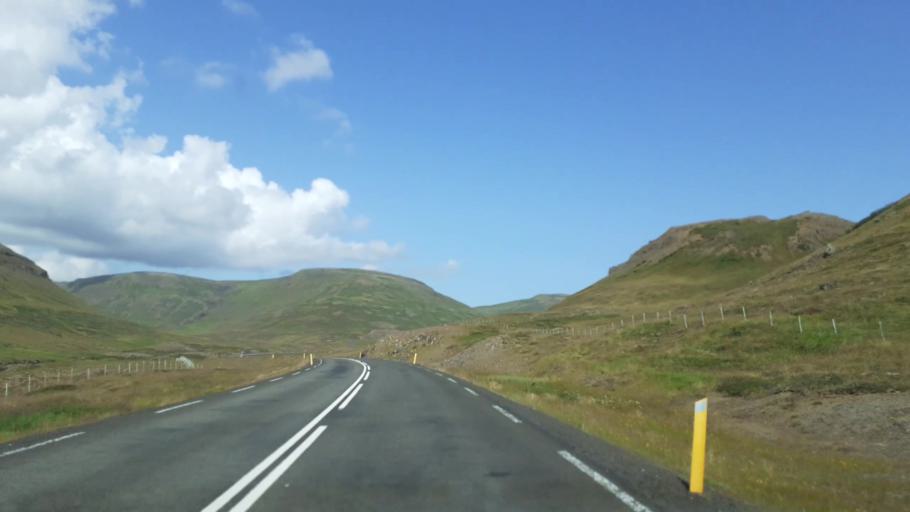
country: IS
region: West
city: Borgarnes
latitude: 64.8252
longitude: -21.4789
